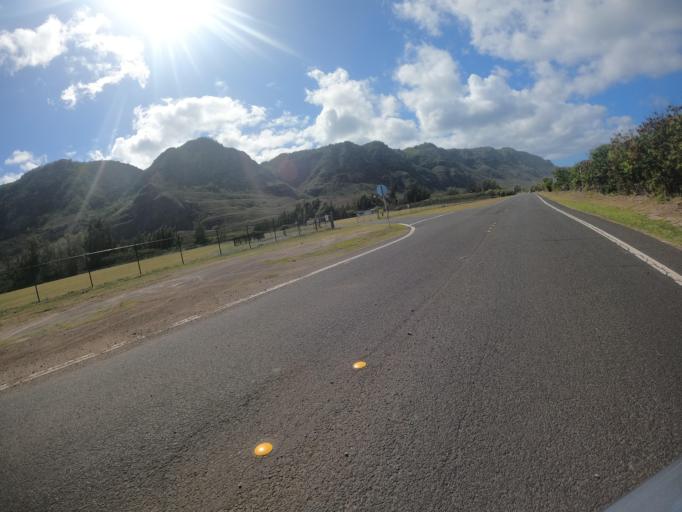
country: US
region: Hawaii
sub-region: Honolulu County
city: Mokuleia
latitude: 21.5807
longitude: -158.2120
